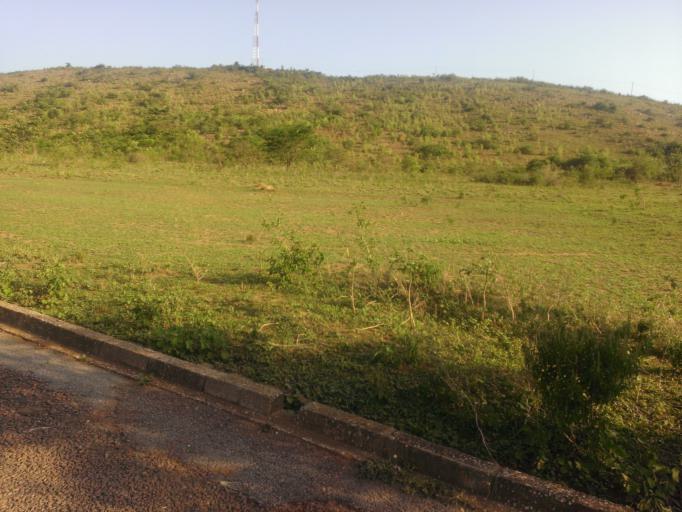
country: UG
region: Eastern Region
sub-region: Busia District
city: Busia
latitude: 0.5453
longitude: 34.0168
